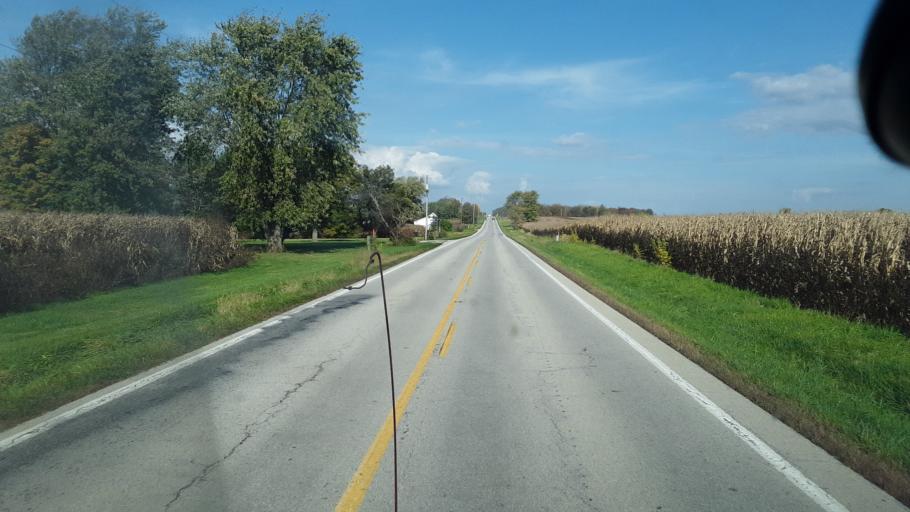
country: US
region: Ohio
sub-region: Clinton County
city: Sabina
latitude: 39.5239
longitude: -83.6975
